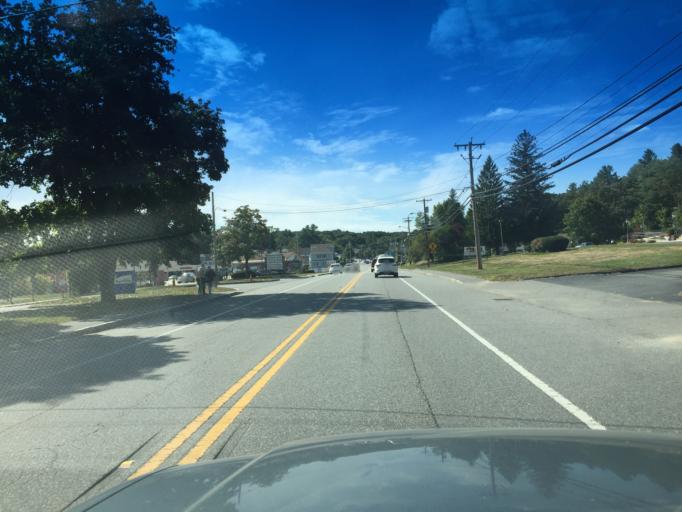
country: US
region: Massachusetts
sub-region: Worcester County
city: Northborough
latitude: 42.3106
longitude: -71.6551
